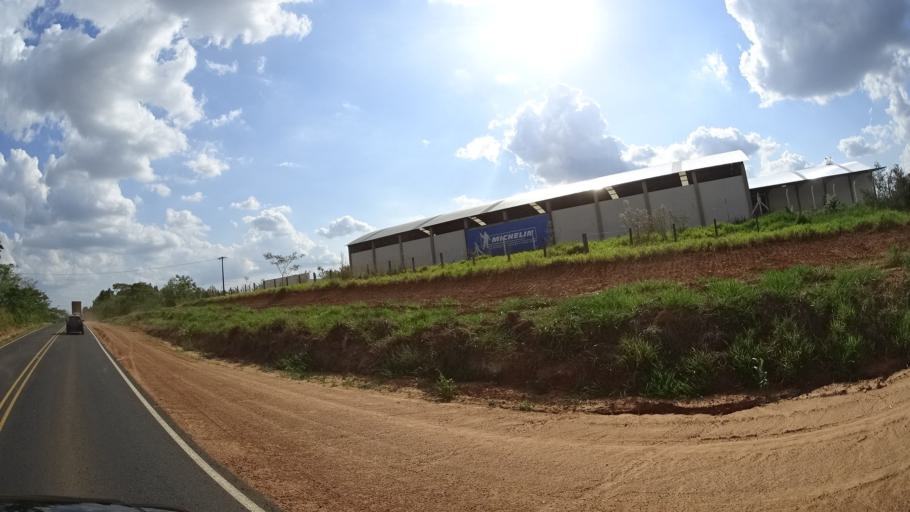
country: BR
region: Sao Paulo
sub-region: Urupes
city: Urupes
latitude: -21.1635
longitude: -49.2873
